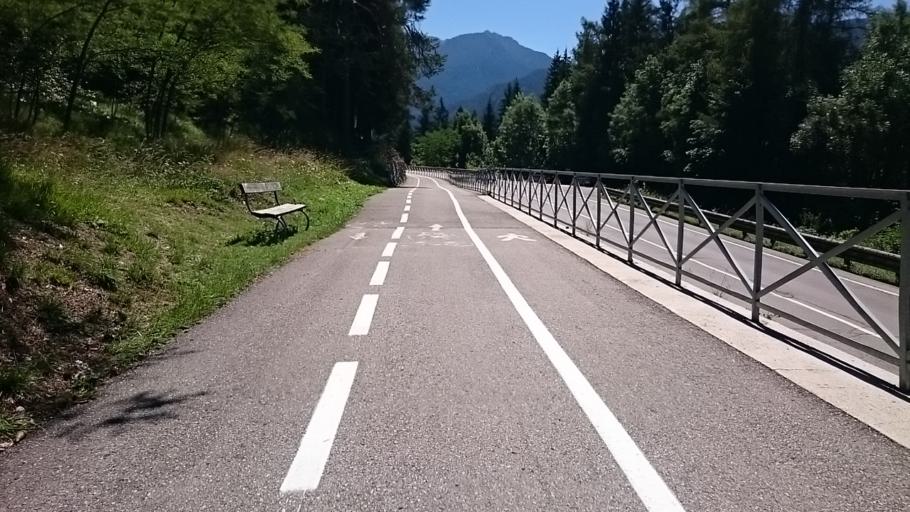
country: IT
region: Veneto
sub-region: Provincia di Belluno
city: Borca
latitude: 46.4442
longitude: 12.2125
